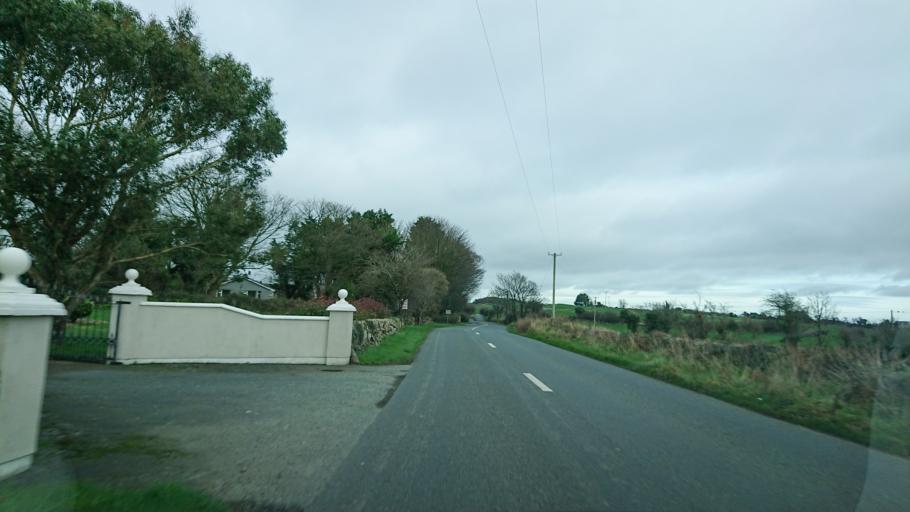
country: IE
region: Leinster
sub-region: Kilkenny
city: Mooncoin
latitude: 52.1943
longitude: -7.2739
